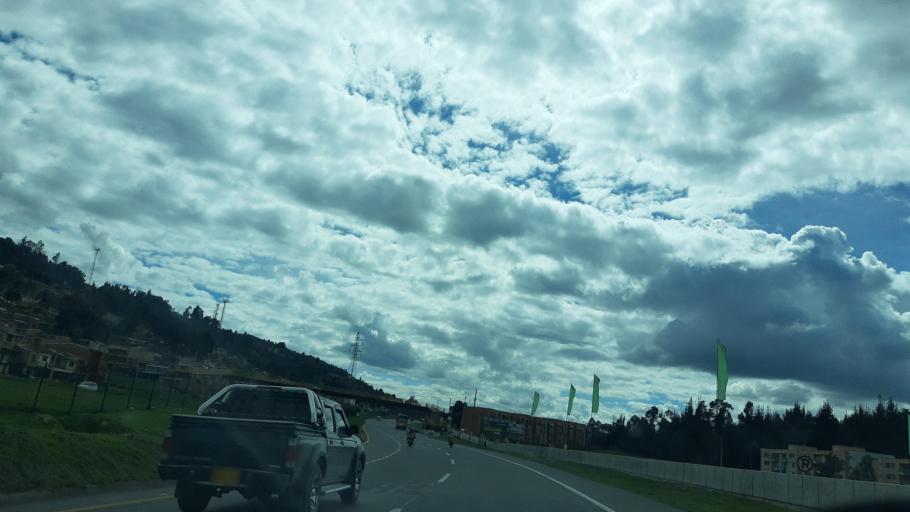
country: CO
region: Cundinamarca
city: Tocancipa
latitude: 4.9641
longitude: -73.9091
